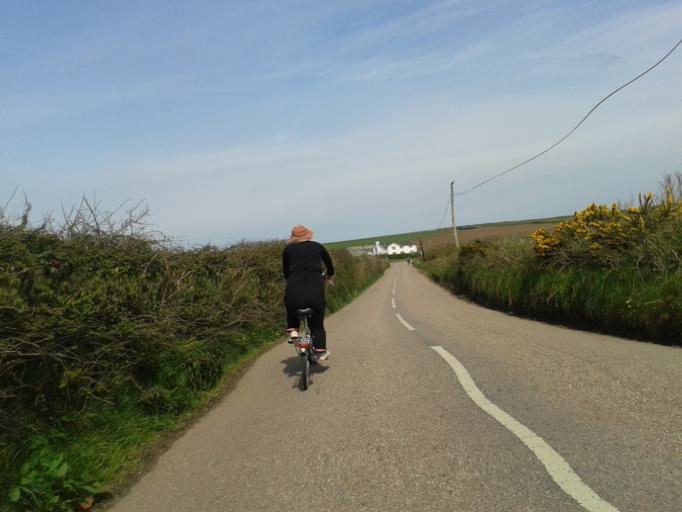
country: GB
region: England
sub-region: Devon
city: Braunton
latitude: 51.1583
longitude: -4.1947
